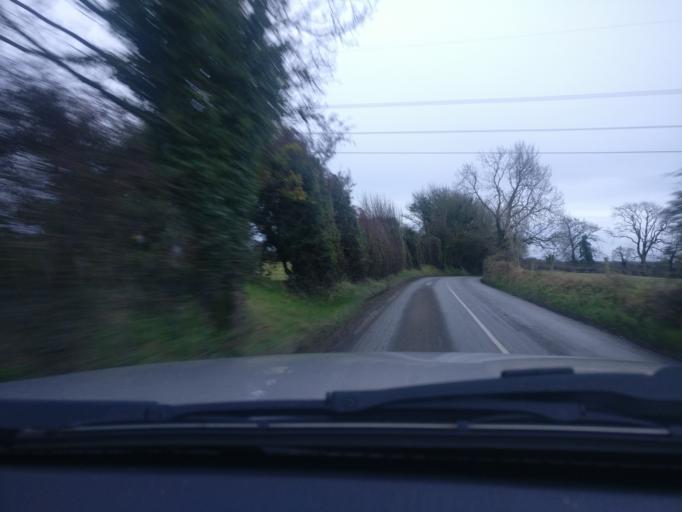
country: IE
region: Leinster
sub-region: Kildare
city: Kilcock
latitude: 53.4718
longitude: -6.6246
